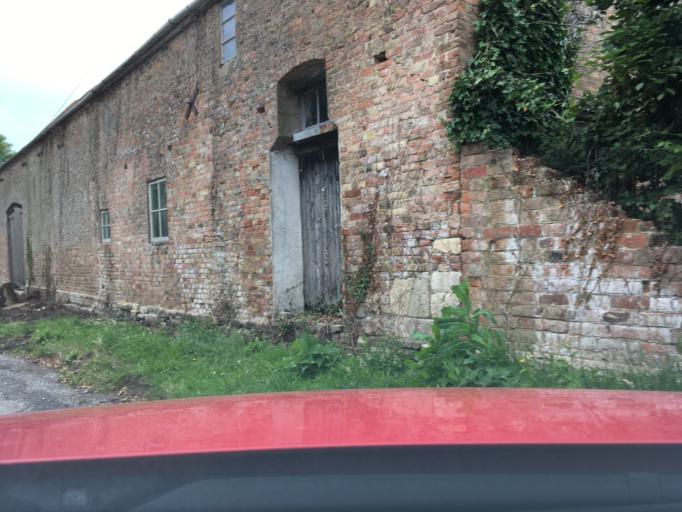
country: GB
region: England
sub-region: Gloucestershire
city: Cinderford
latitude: 51.7929
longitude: -2.4274
